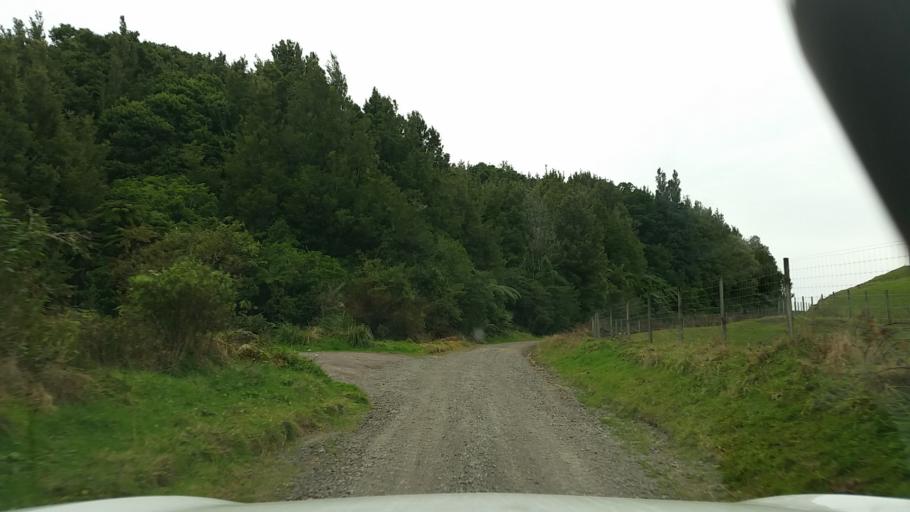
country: NZ
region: Bay of Plenty
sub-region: Rotorua District
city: Rotorua
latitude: -38.1572
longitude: 176.3723
